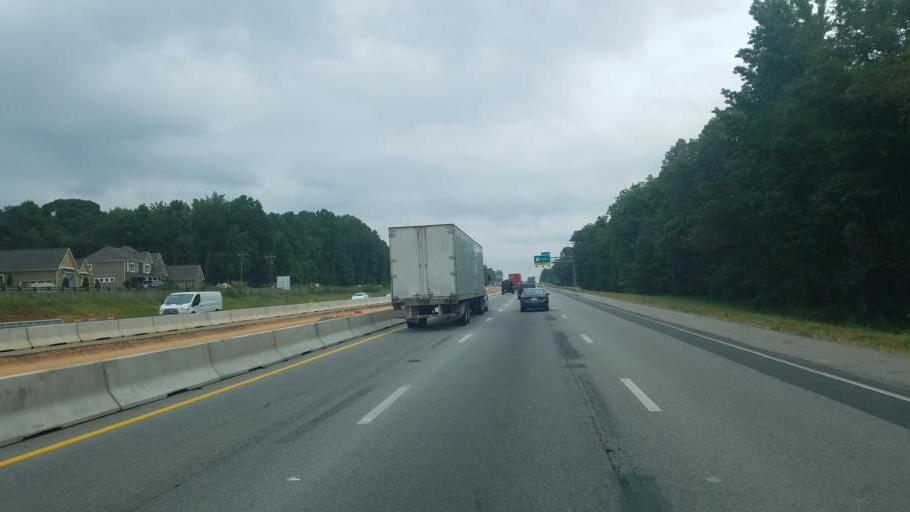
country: US
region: North Carolina
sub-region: Gaston County
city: Davidson
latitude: 35.5417
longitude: -80.8597
